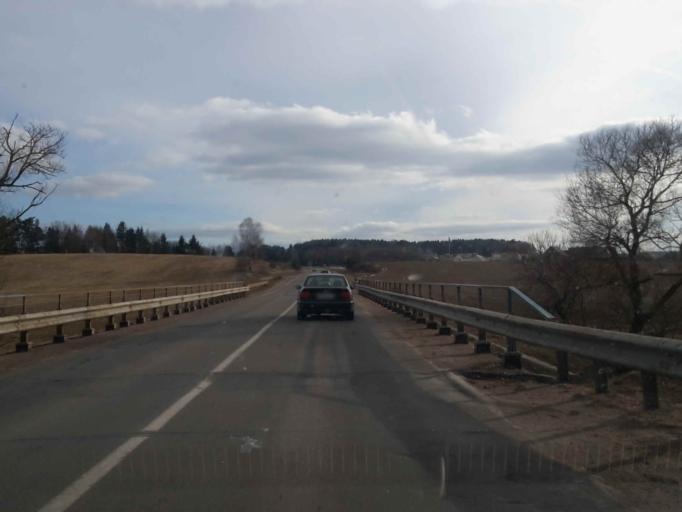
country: BY
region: Minsk
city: Bal'shavik
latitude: 54.0363
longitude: 27.5609
